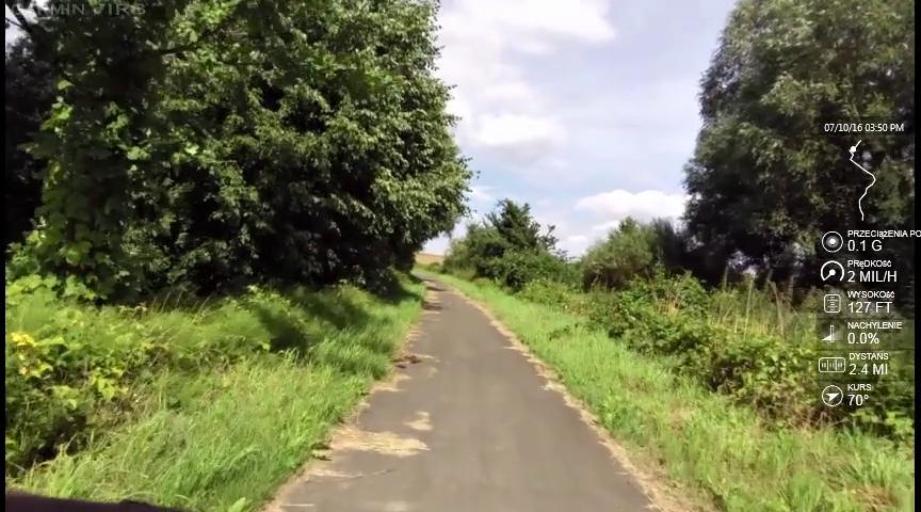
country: PL
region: West Pomeranian Voivodeship
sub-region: Powiat gryfinski
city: Banie
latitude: 53.1411
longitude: 14.6181
